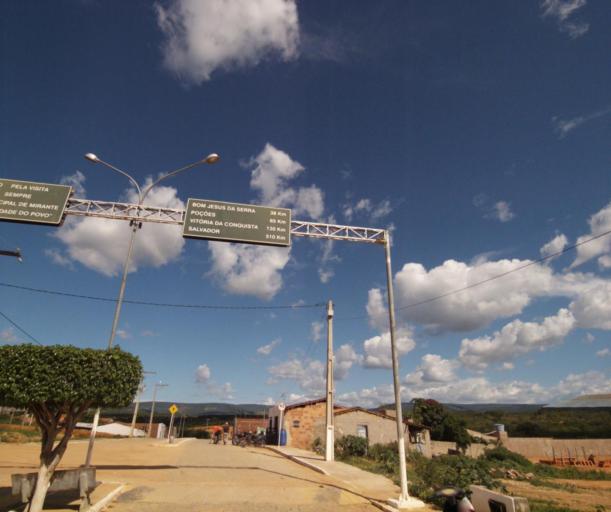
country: BR
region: Bahia
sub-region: Pocoes
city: Pocoes
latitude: -14.2425
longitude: -40.7644
